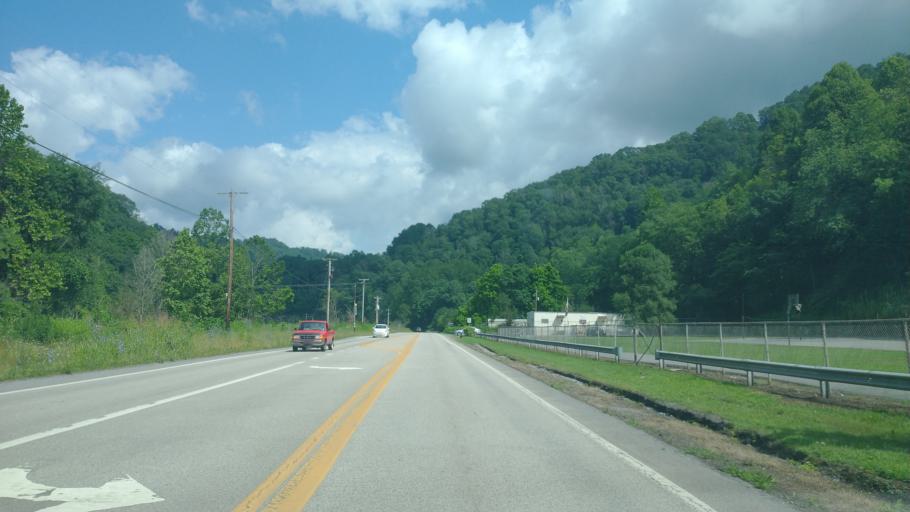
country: US
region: West Virginia
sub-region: McDowell County
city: Welch
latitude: 37.4207
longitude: -81.4983
